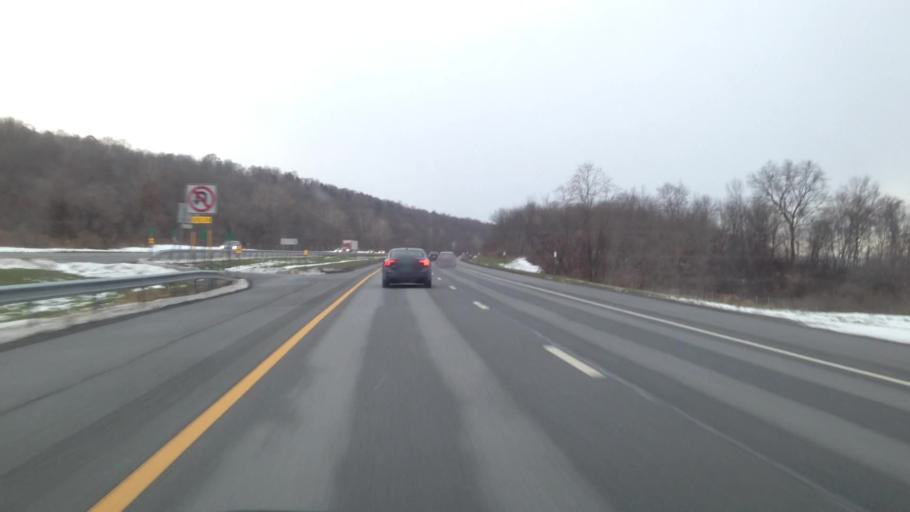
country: US
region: New York
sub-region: Montgomery County
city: Saint Johnsville
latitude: 42.9894
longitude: -74.7200
